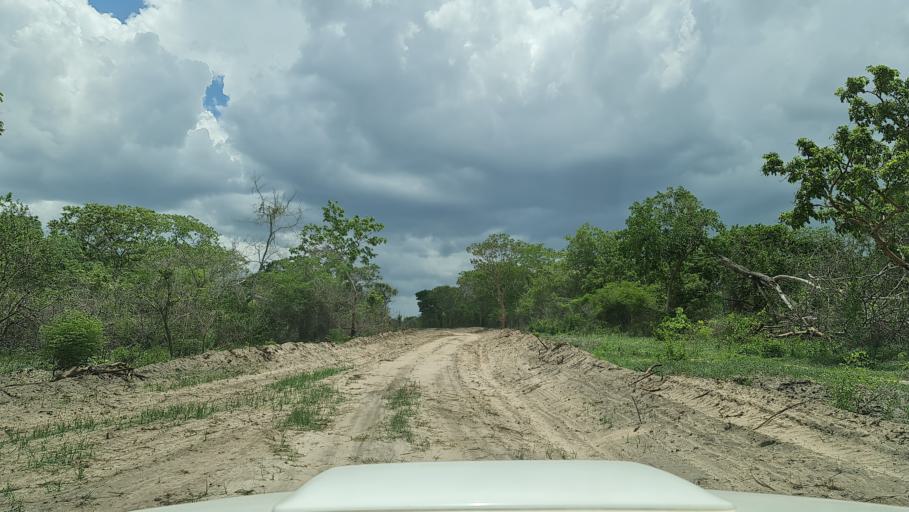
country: MZ
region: Nampula
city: Ilha de Mocambique
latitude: -15.2449
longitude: 40.3649
